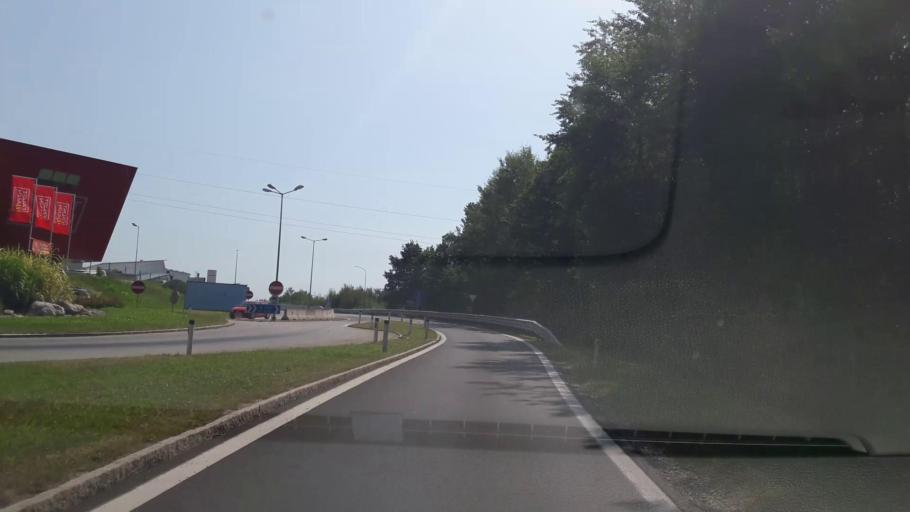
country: AT
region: Styria
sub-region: Politischer Bezirk Hartberg-Fuerstenfeld
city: Sankt Johann in der Haide
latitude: 47.2797
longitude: 16.0069
